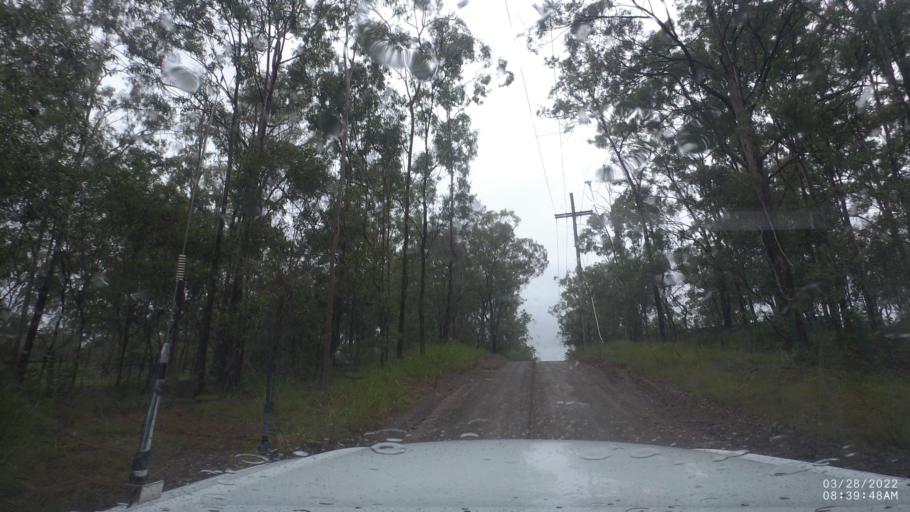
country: AU
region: Queensland
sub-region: Logan
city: Cedar Vale
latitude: -27.8362
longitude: 153.0647
